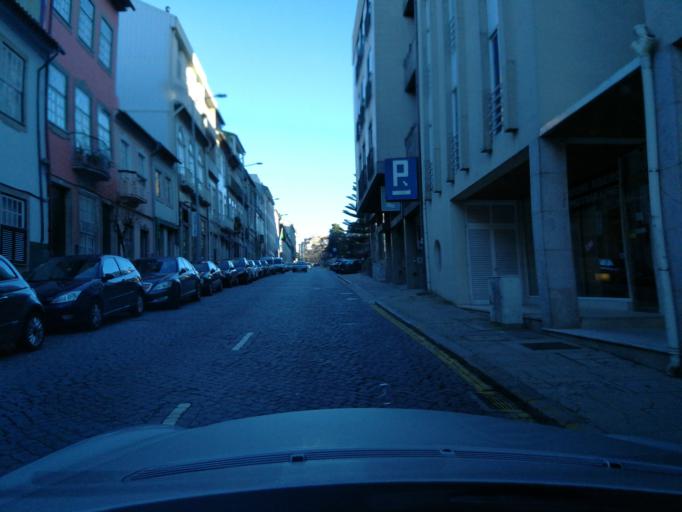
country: PT
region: Braga
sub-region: Braga
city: Braga
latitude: 41.5525
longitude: -8.4171
